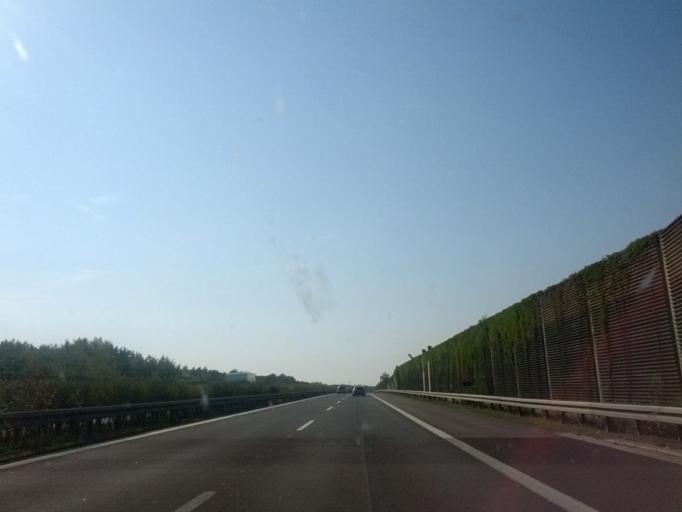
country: DE
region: Brandenburg
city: Bernau bei Berlin
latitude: 52.6730
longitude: 13.5665
